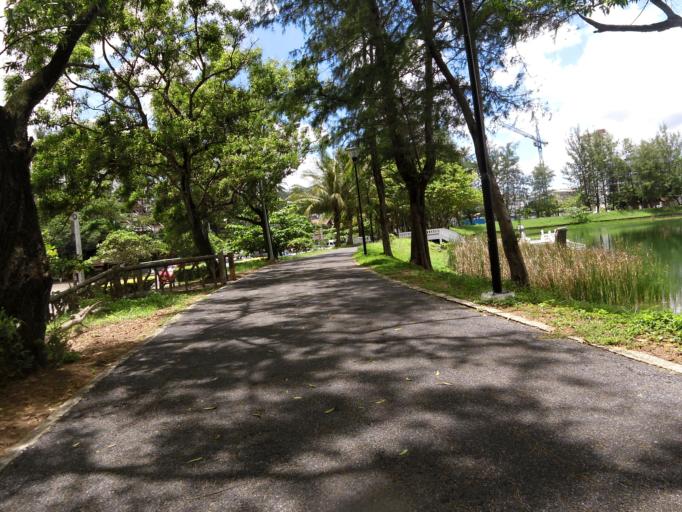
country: TH
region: Phuket
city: Ban Karon
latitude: 7.8525
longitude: 98.2943
